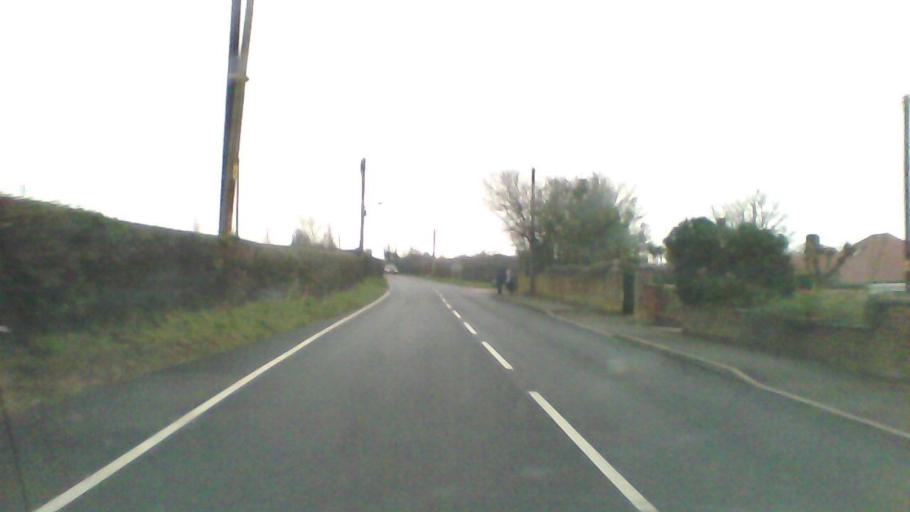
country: GB
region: England
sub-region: Isle of Wight
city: Newport
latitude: 50.6989
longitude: -1.2689
